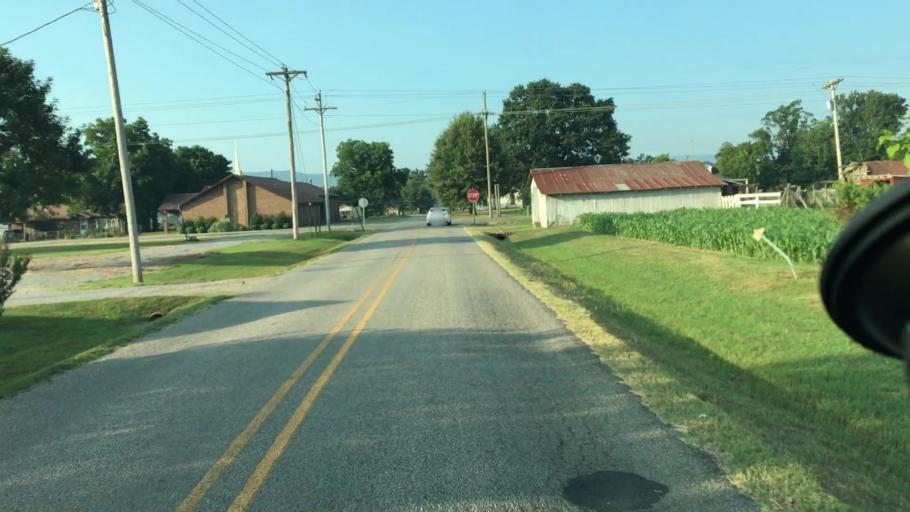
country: US
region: Arkansas
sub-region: Johnson County
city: Coal Hill
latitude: 35.3378
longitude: -93.6139
